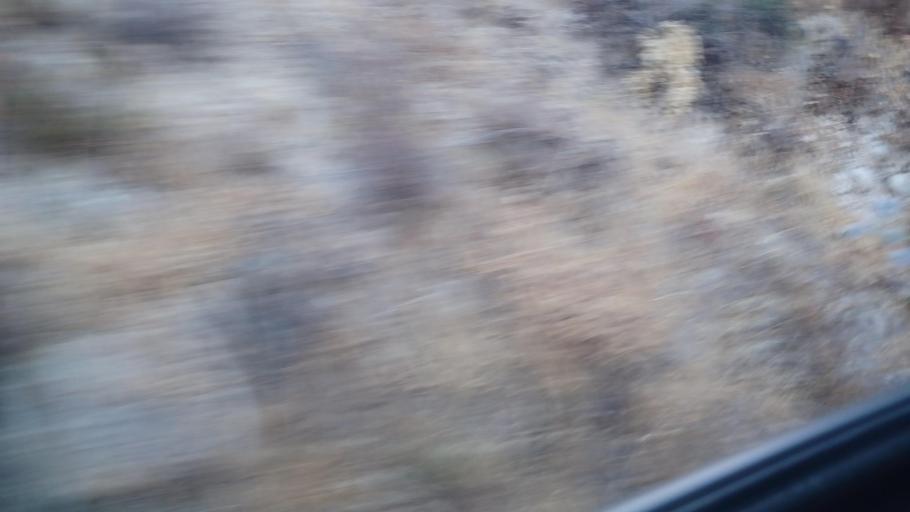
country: CY
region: Pafos
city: Mesogi
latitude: 34.8290
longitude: 32.5759
